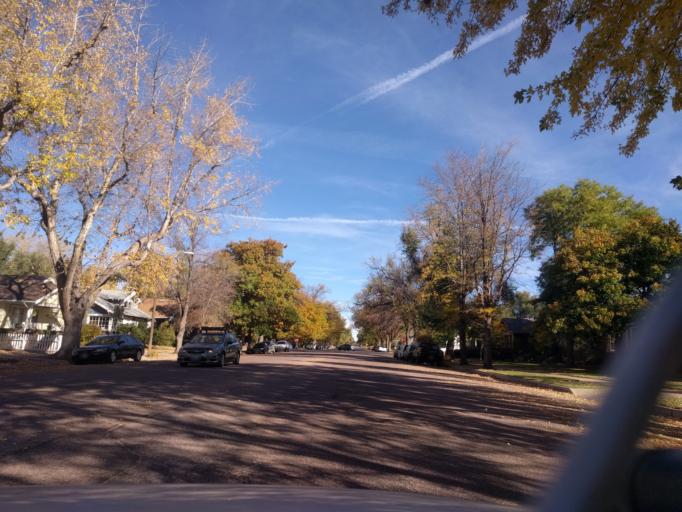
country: US
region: Colorado
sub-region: El Paso County
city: Colorado Springs
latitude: 38.8494
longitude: -104.8155
